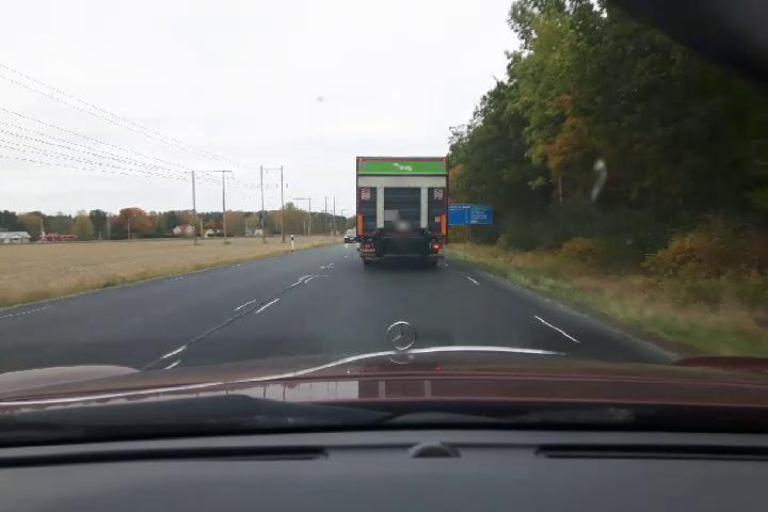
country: SE
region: Uppsala
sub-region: Enkopings Kommun
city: Enkoping
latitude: 59.6348
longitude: 17.0510
